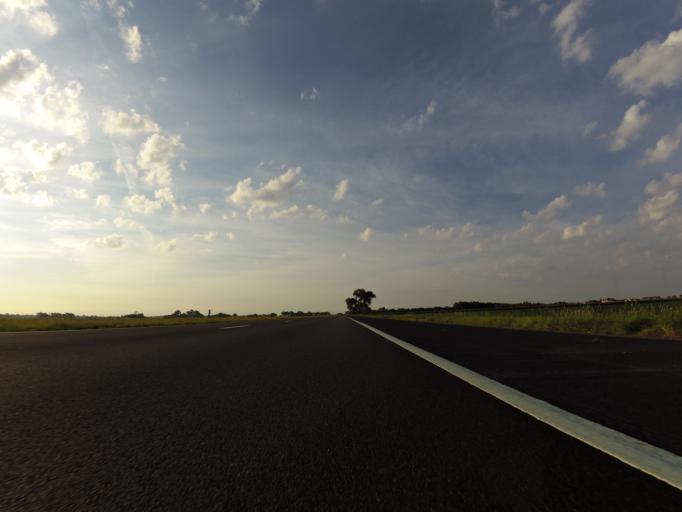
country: US
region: Kansas
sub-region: Sedgwick County
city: Colwich
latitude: 37.8206
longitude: -97.5113
